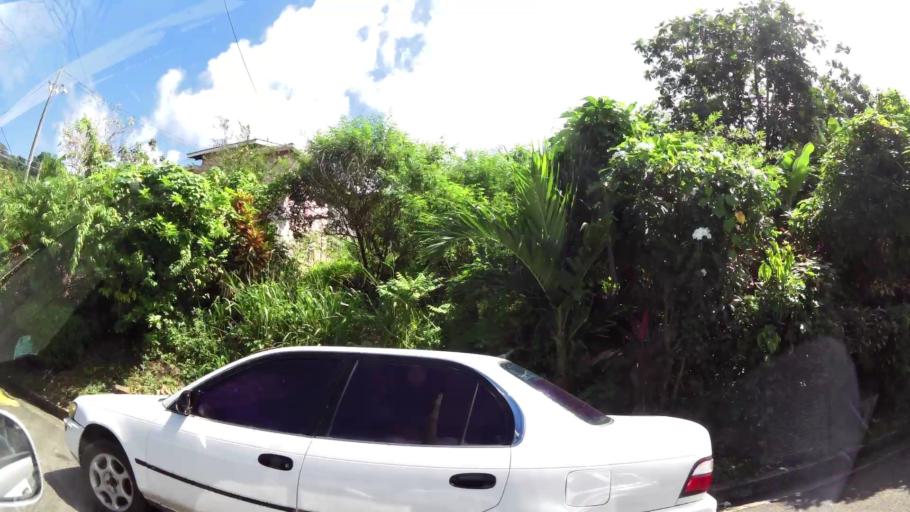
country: GD
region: Saint Mark
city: Victoria
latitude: 12.2138
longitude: -61.6899
